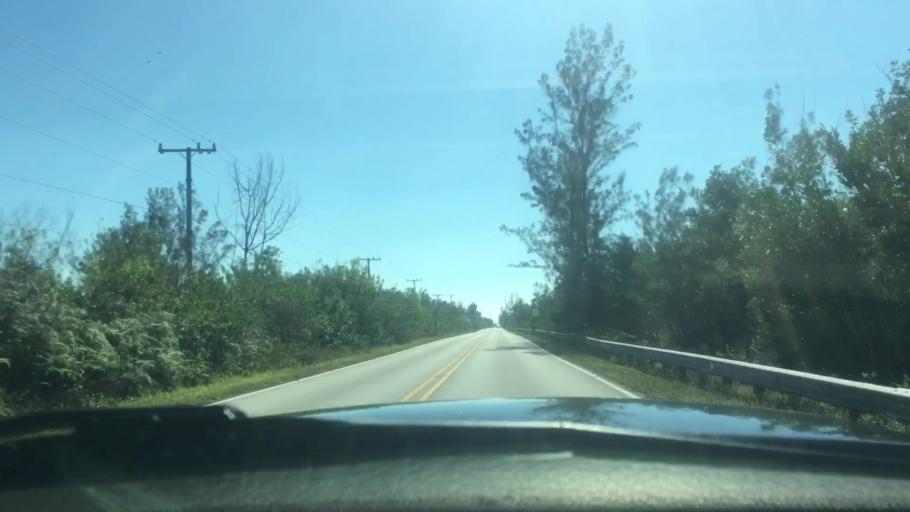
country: US
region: Florida
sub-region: Miami-Dade County
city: Florida City
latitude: 25.3720
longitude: -80.4332
